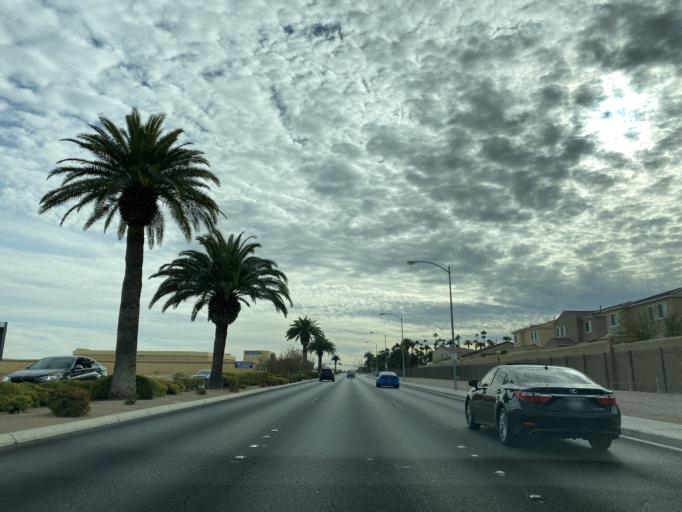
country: US
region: Nevada
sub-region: Clark County
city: Enterprise
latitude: 36.0516
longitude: -115.2792
